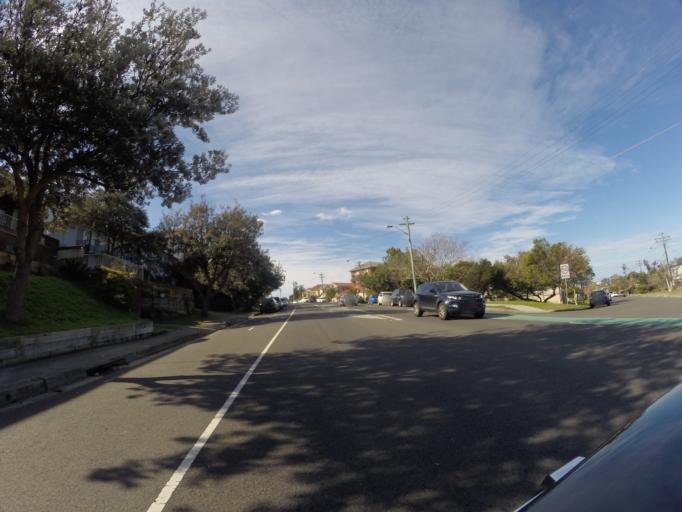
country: AU
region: New South Wales
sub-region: Randwick
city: South Coogee
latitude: -33.9402
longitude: 151.2552
